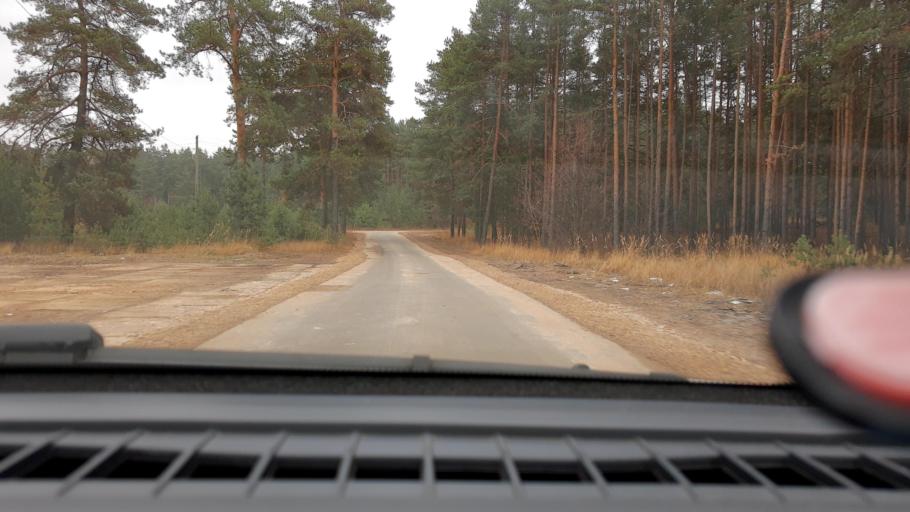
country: RU
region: Nizjnij Novgorod
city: Lukino
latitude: 56.3905
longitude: 43.7167
